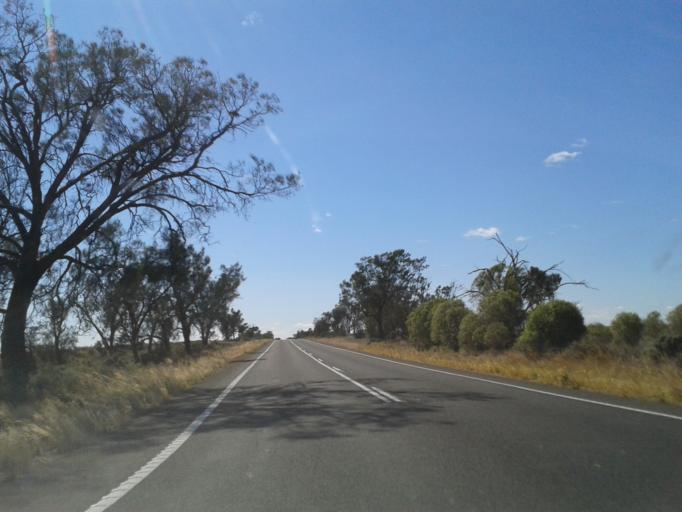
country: AU
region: New South Wales
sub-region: Wentworth
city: Dareton
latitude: -34.2759
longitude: 141.4910
